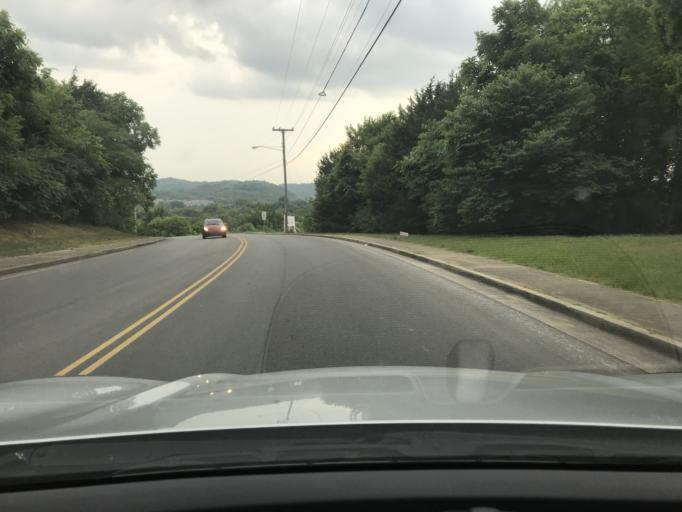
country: US
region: Tennessee
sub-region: Davidson County
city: Goodlettsville
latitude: 36.2982
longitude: -86.7151
